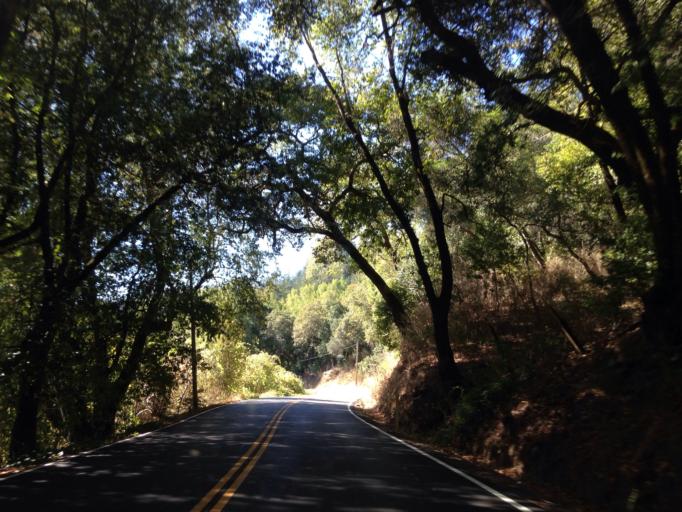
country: US
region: California
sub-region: Sonoma County
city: Forestville
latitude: 38.5106
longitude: -122.9122
